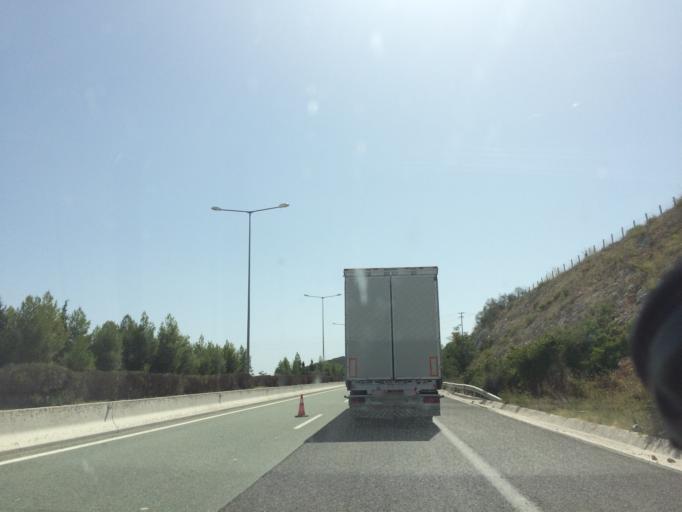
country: GR
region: Thessaly
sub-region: Nomos Magnisias
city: Pteleos
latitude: 39.0219
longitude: 22.9142
